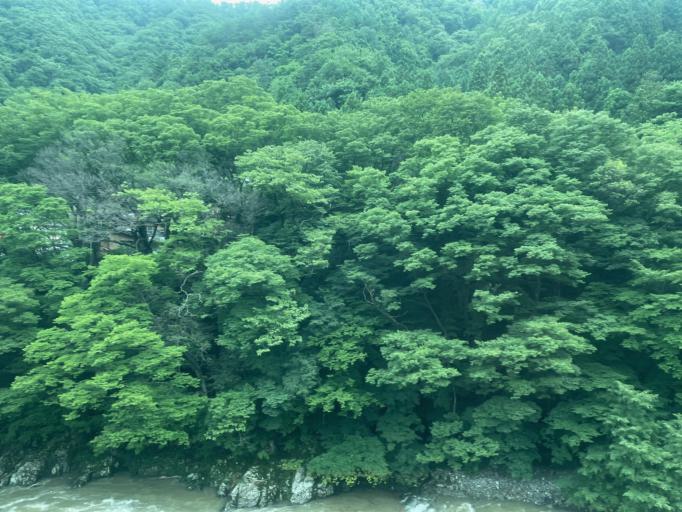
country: JP
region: Gunma
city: Numata
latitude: 36.7830
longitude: 138.9727
